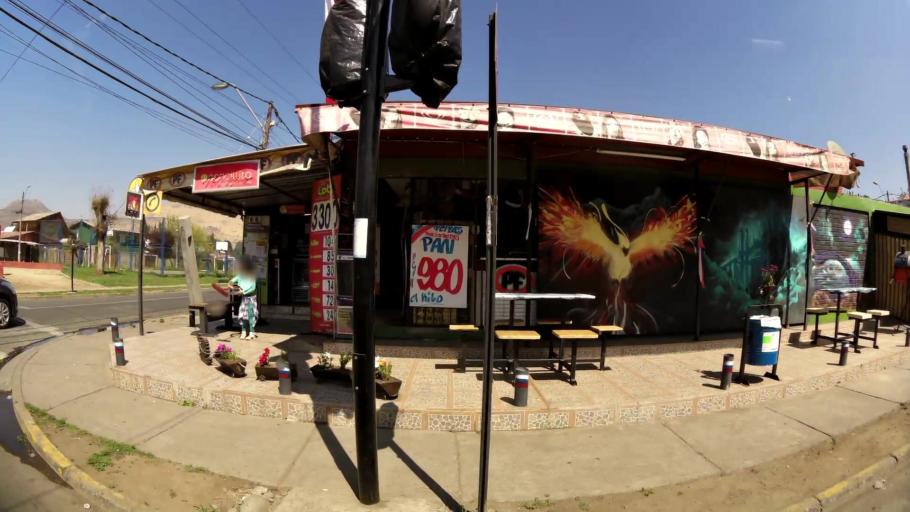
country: CL
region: Santiago Metropolitan
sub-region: Provincia de Santiago
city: Lo Prado
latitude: -33.3682
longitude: -70.7203
